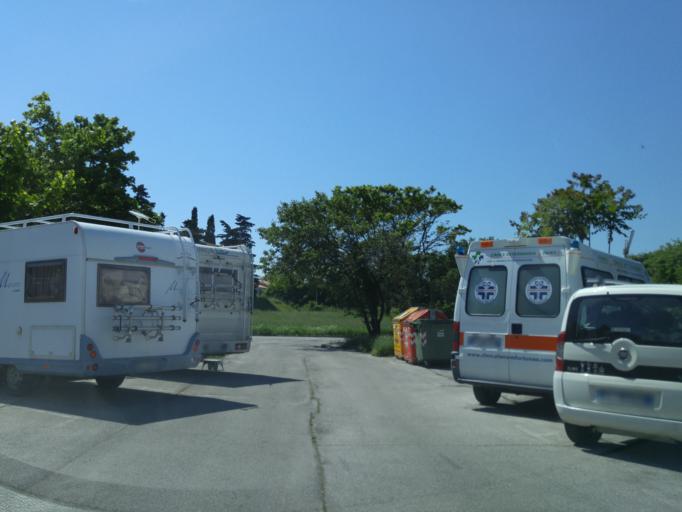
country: IT
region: The Marches
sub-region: Provincia di Pesaro e Urbino
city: Fano
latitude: 43.8459
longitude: 13.0106
